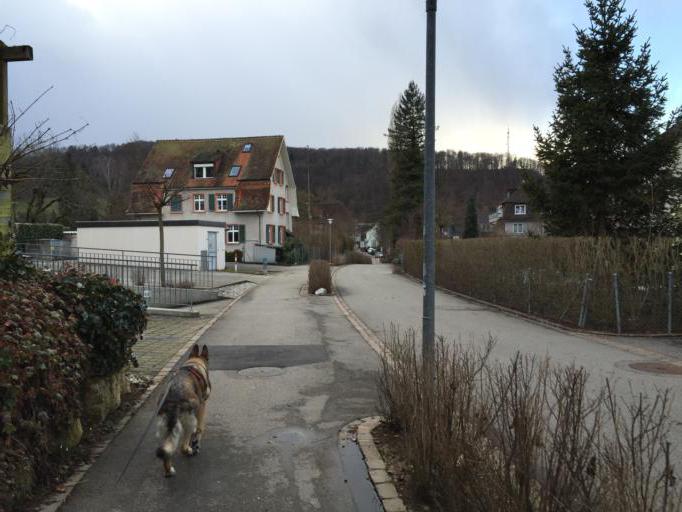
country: CH
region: Basel-Landschaft
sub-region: Bezirk Sissach
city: Sissach
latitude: 47.4600
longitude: 7.8114
